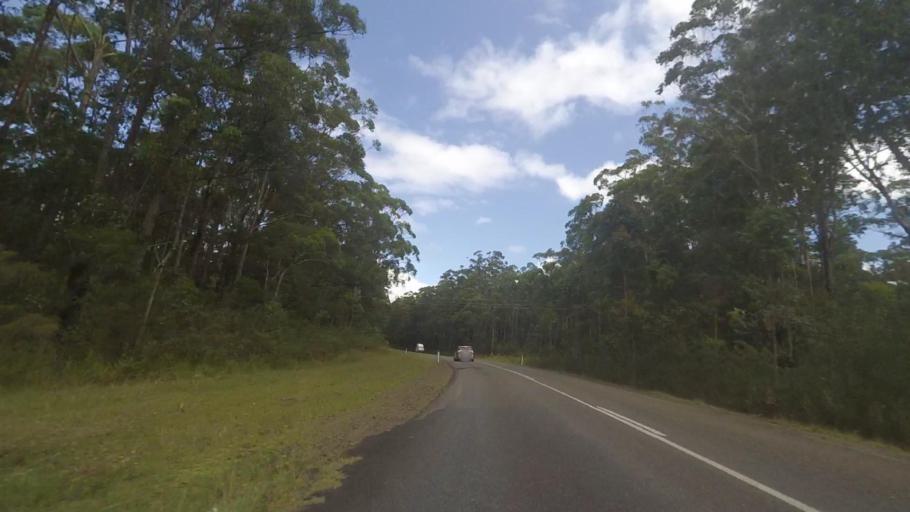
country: AU
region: New South Wales
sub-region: Great Lakes
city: Bulahdelah
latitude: -32.3974
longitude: 152.2537
